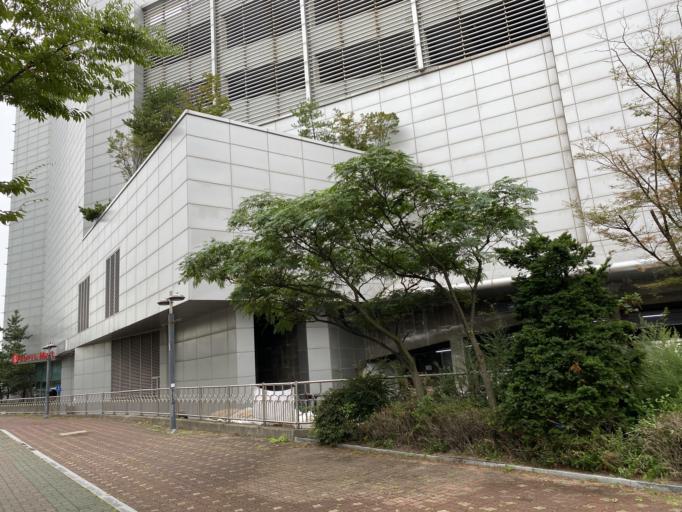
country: KR
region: Incheon
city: Incheon
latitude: 37.4929
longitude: 126.4922
